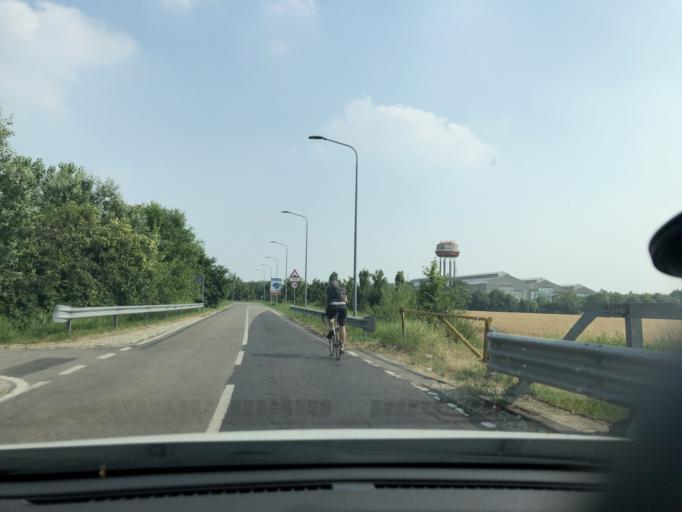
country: IT
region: Lombardy
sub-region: Citta metropolitana di Milano
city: Novegro-Tregarezzo-San Felice
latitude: 45.4859
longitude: 9.2570
